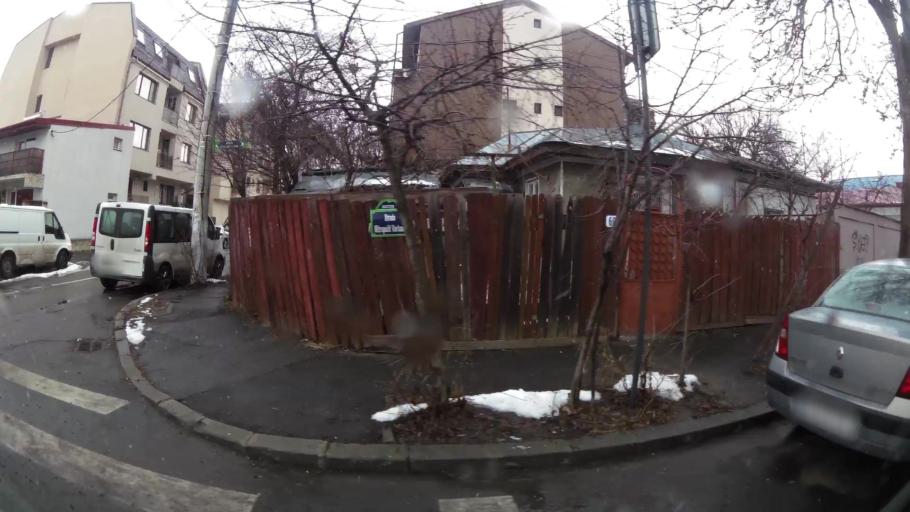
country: RO
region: Ilfov
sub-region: Comuna Chiajna
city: Rosu
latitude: 44.4941
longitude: 26.0369
